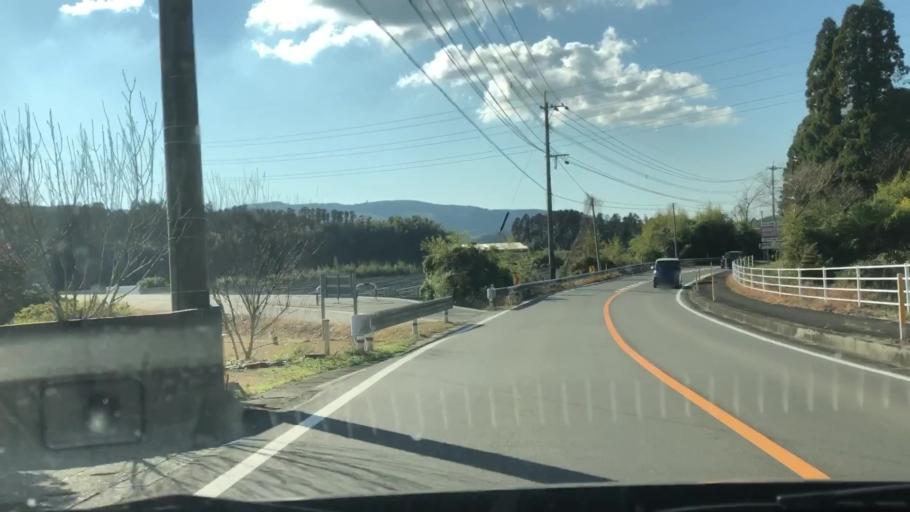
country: JP
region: Kagoshima
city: Satsumasendai
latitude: 31.8564
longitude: 130.3749
